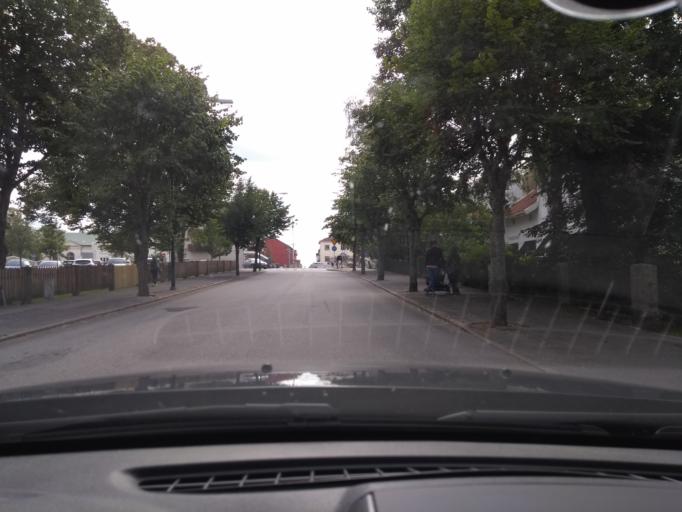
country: SE
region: Kalmar
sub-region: Vimmerby Kommun
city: Vimmerby
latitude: 57.6678
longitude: 15.8573
